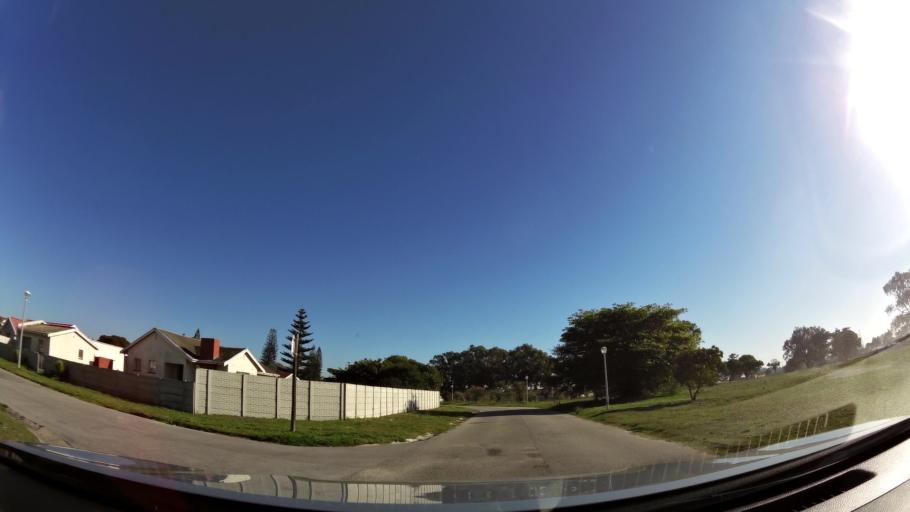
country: ZA
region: Eastern Cape
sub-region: Nelson Mandela Bay Metropolitan Municipality
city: Port Elizabeth
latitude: -33.9879
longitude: 25.6280
